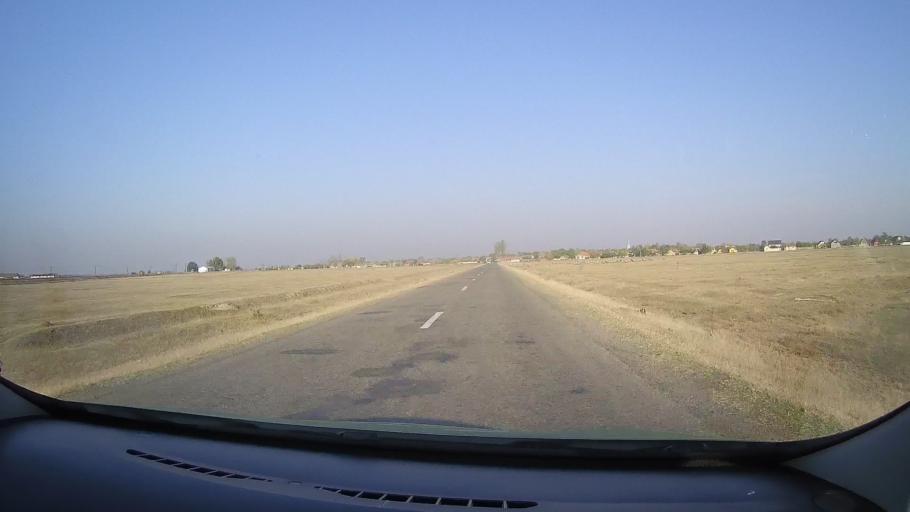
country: RO
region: Arad
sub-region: Comuna Graniceri
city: Graniceri
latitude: 46.5120
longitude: 21.3107
